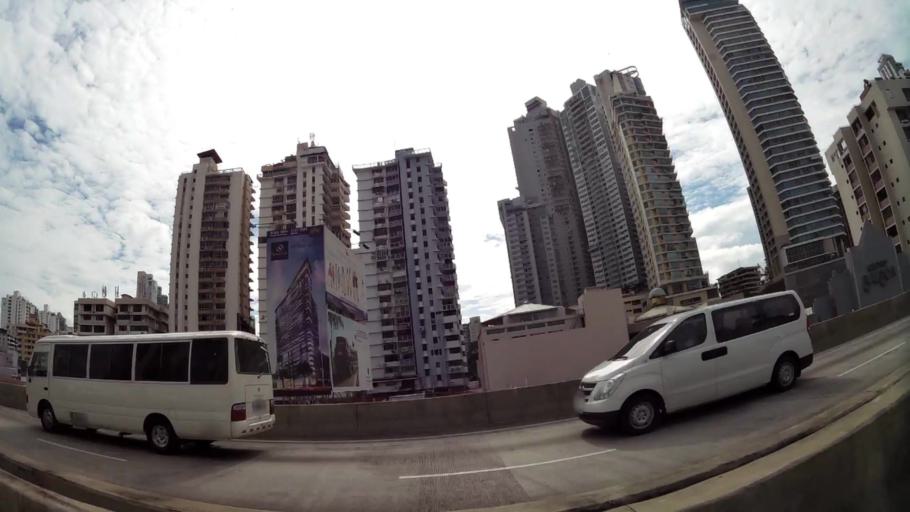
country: PA
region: Panama
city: Panama
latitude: 8.9759
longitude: -79.5166
